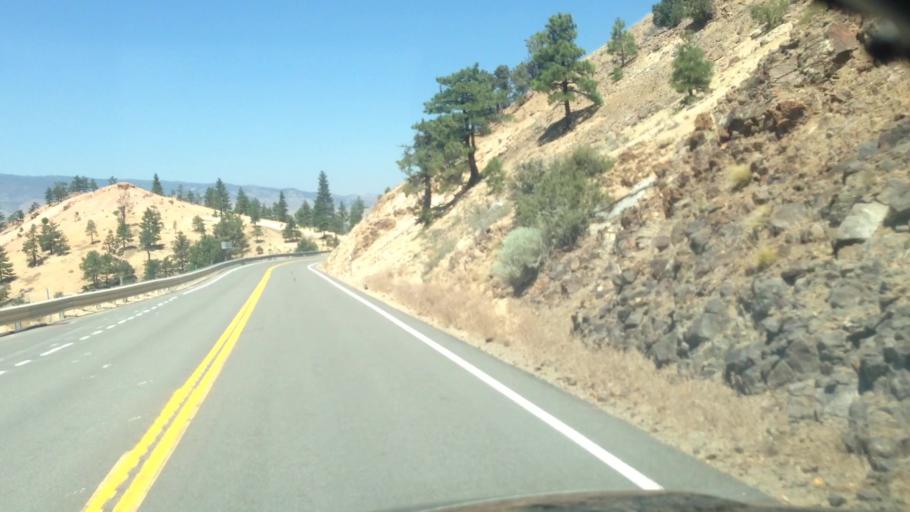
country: US
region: Nevada
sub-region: Storey County
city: Virginia City
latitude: 39.3903
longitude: -119.7011
